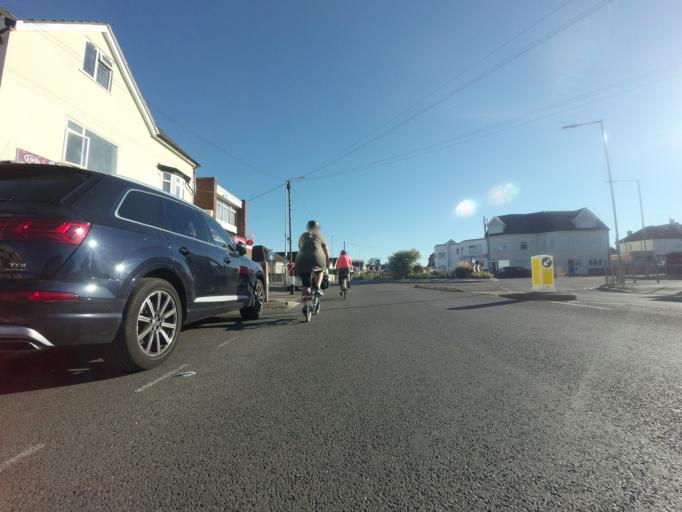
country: GB
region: England
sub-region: Kent
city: Herne Bay
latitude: 51.3661
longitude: 1.1111
